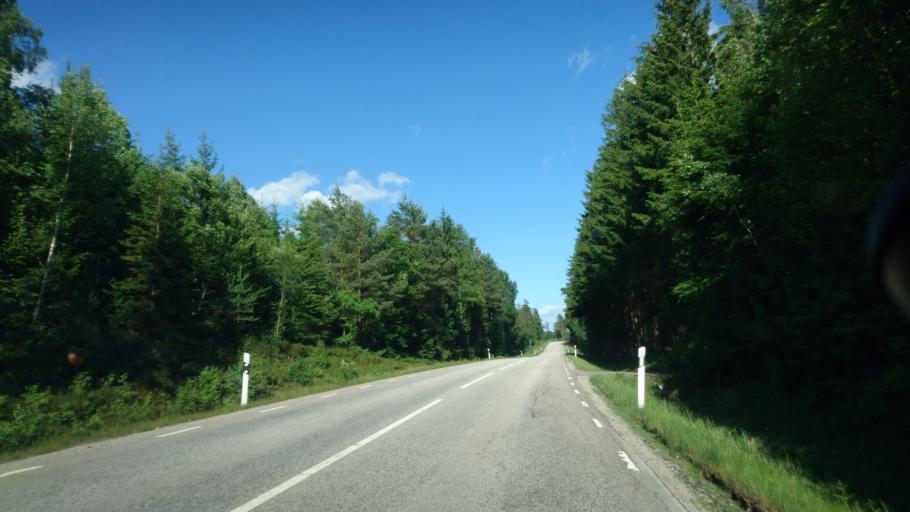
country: SE
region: Skane
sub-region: Osby Kommun
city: Lonsboda
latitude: 56.3906
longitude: 14.4223
